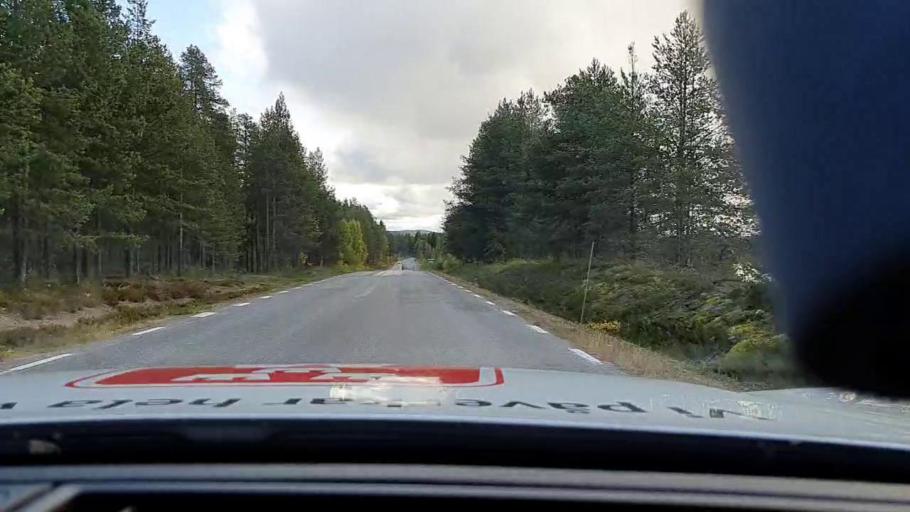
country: SE
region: Vaesterbotten
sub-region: Skelleftea Kommun
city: Langsele
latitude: 64.9593
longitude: 19.9022
